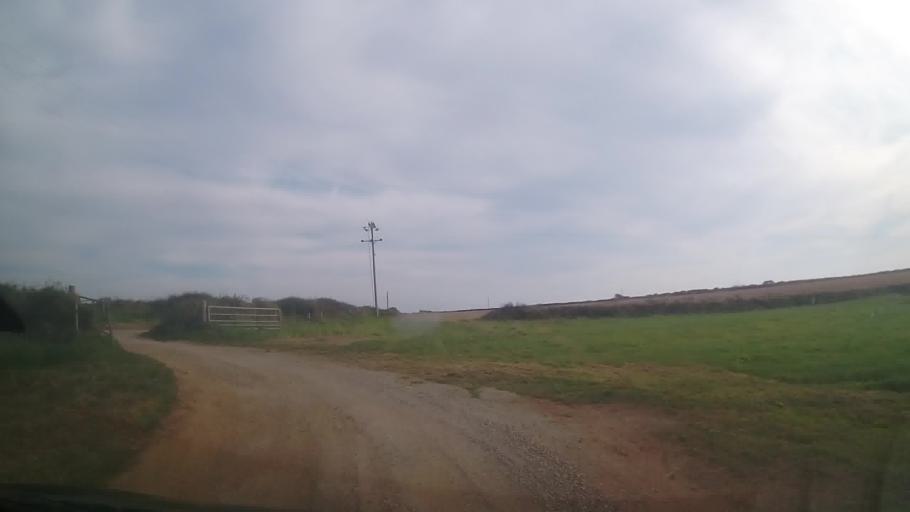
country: GB
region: Wales
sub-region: Pembrokeshire
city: Llanrhian
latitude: 51.9237
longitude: -5.2191
